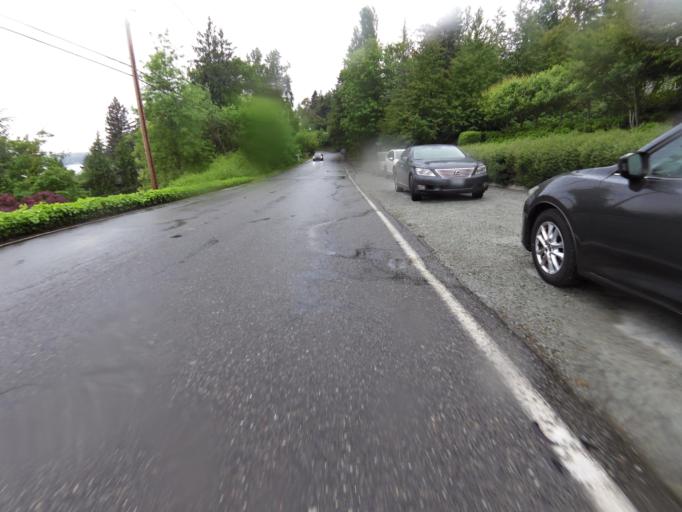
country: US
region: Washington
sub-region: King County
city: Bryn Mawr-Skyway
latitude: 47.5290
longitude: -122.2321
